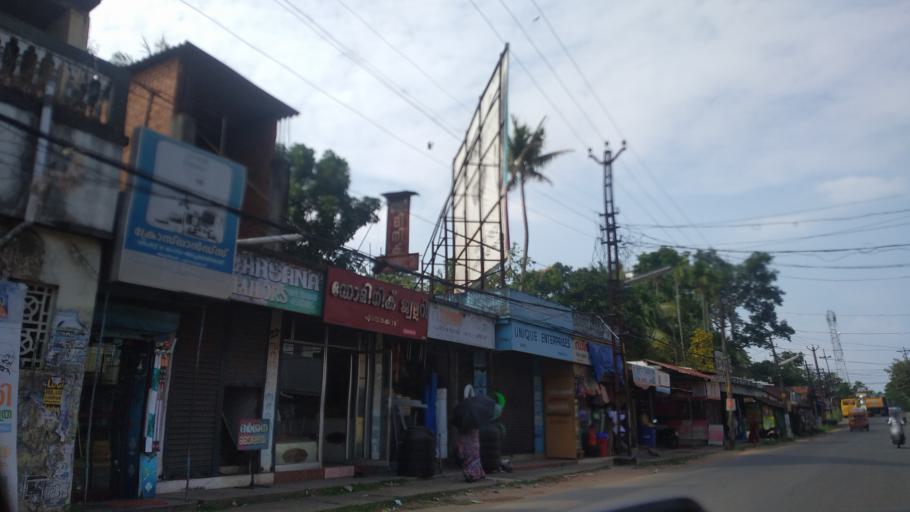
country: IN
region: Kerala
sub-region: Ernakulam
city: Elur
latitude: 10.0790
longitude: 76.2102
